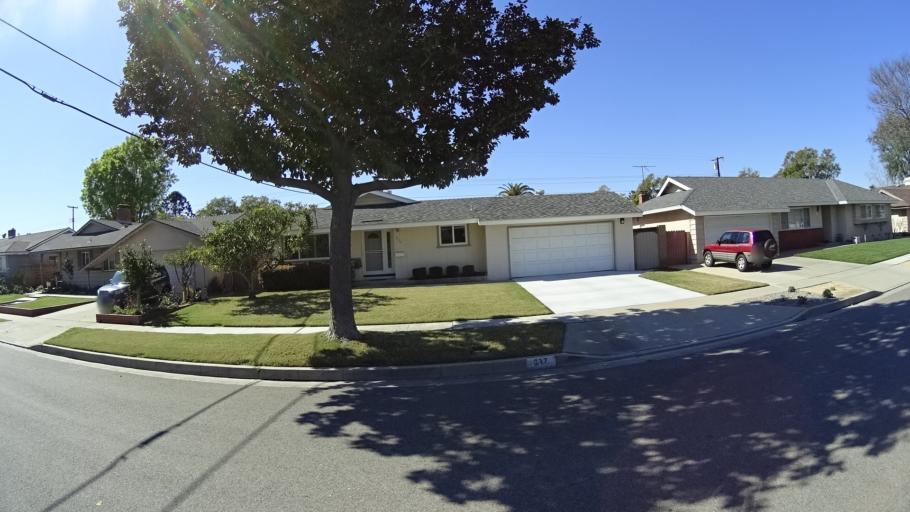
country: US
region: California
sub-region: Orange County
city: Anaheim
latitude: 33.8298
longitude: -117.8734
